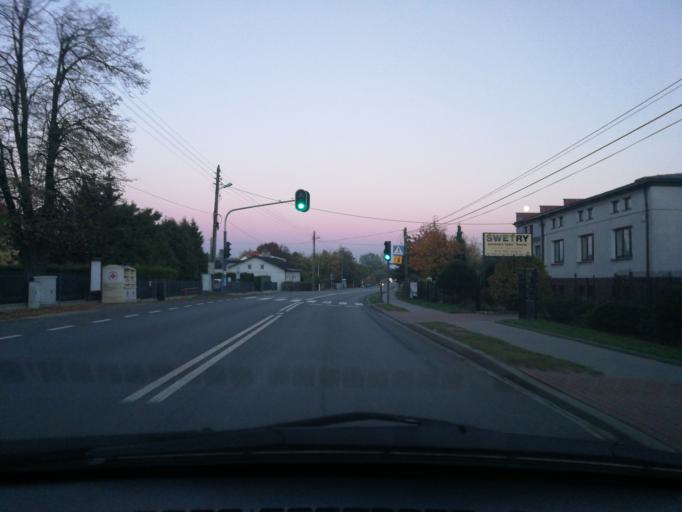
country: PL
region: Lodz Voivodeship
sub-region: Powiat brzezinski
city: Brzeziny
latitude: 51.8063
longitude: 19.6712
